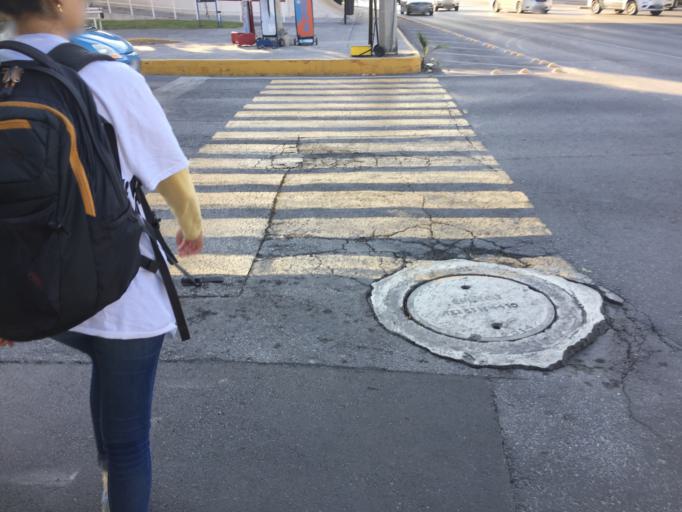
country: MX
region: Nuevo Leon
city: Garza Garcia
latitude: 25.6514
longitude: -100.3712
